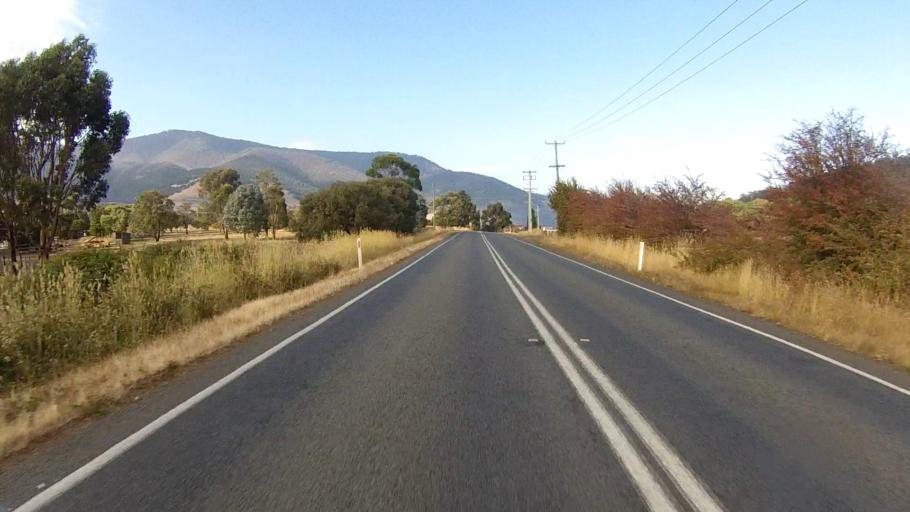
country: AU
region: Tasmania
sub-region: Brighton
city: Bridgewater
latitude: -42.7329
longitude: 147.1765
